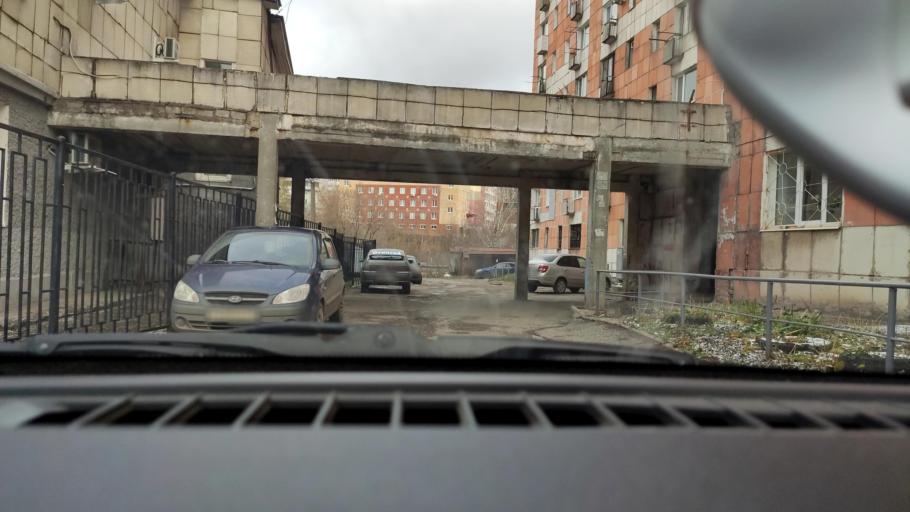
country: RU
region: Perm
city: Perm
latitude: 57.9916
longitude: 56.2384
